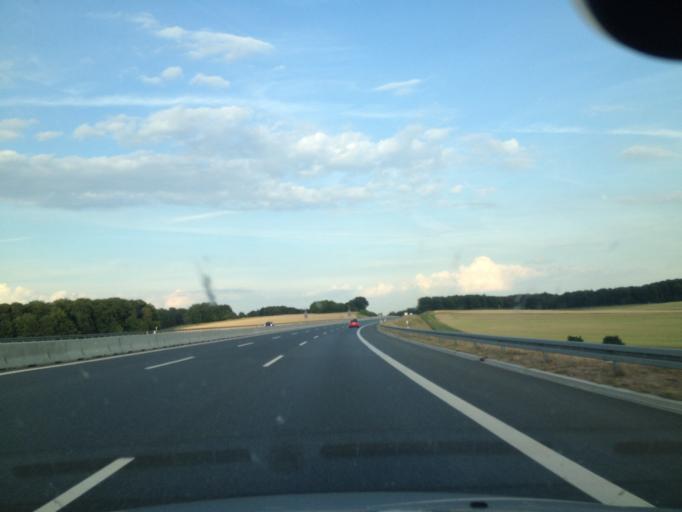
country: DE
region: Bavaria
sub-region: Regierungsbezirk Unterfranken
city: Uettingen
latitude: 49.7754
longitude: 9.7335
